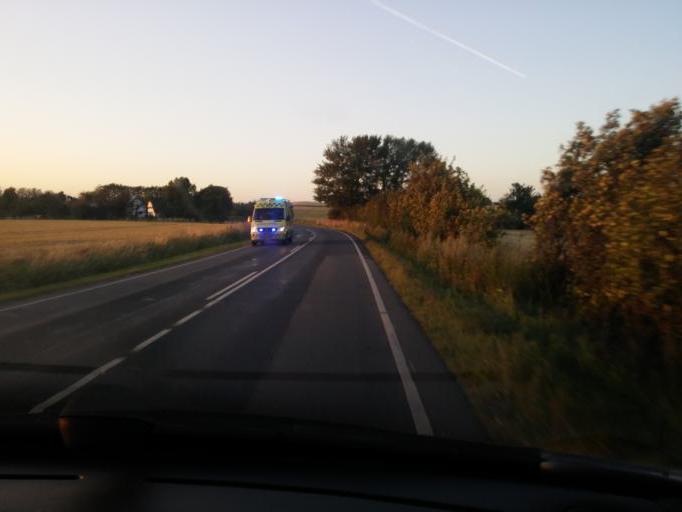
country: DK
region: South Denmark
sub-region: Langeland Kommune
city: Rudkobing
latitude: 54.8731
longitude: 10.7341
